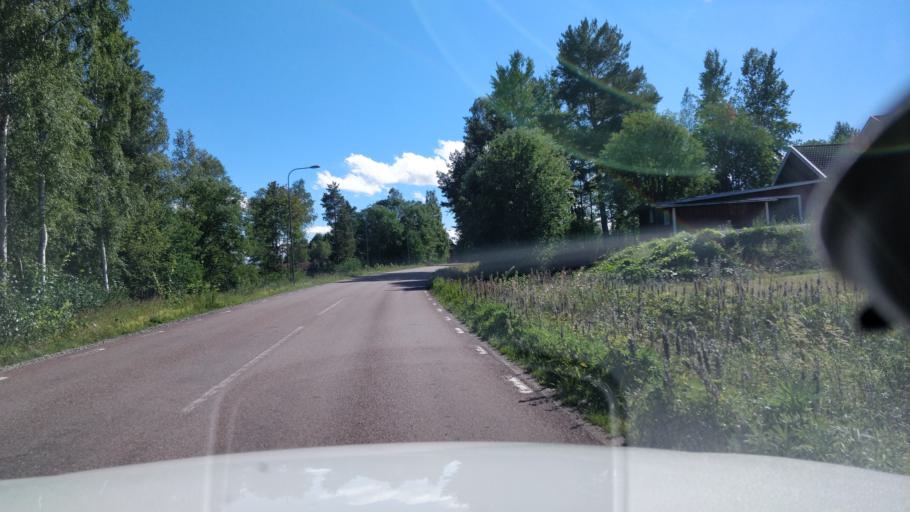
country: SE
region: Dalarna
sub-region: Faluns Kommun
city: Bjursas
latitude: 60.7430
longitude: 15.4688
